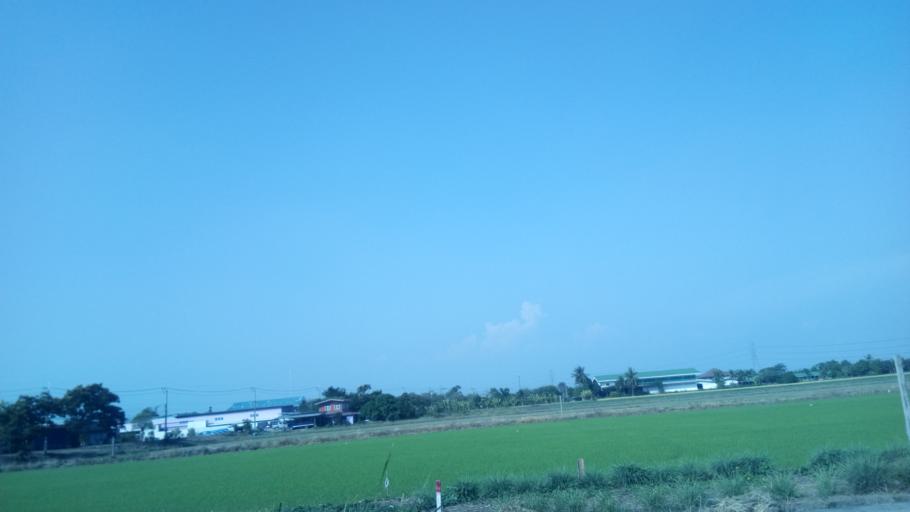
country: TH
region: Nonthaburi
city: Sai Noi
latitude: 13.9427
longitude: 100.3314
